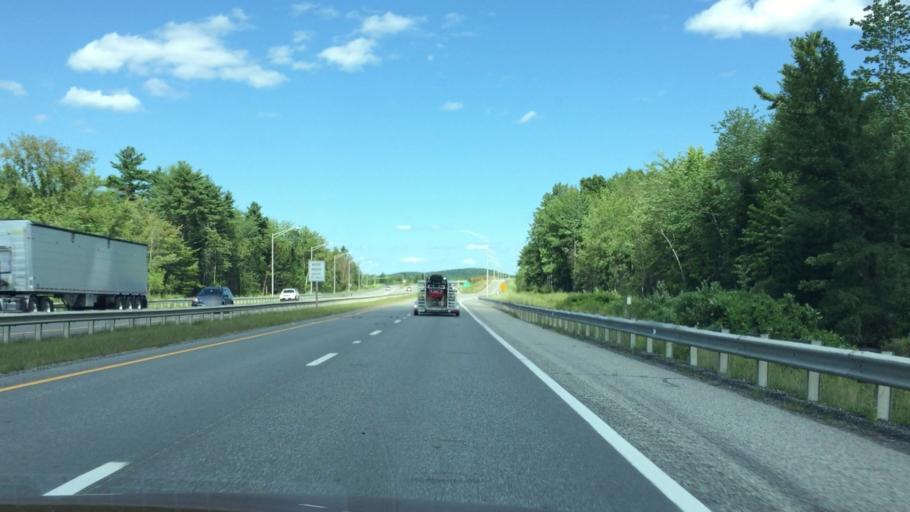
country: US
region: Maine
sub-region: Androscoggin County
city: Sabattus
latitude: 44.0964
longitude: -70.0931
